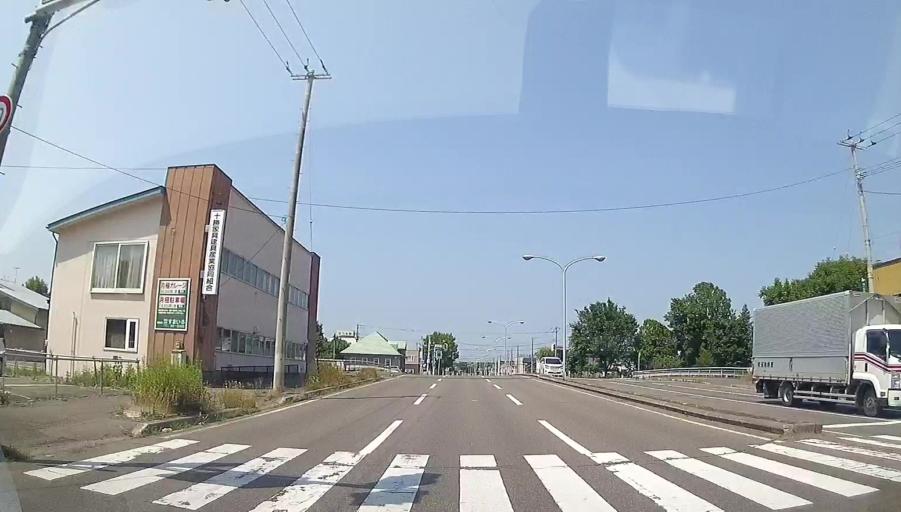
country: JP
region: Hokkaido
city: Obihiro
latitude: 42.9282
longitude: 143.1996
